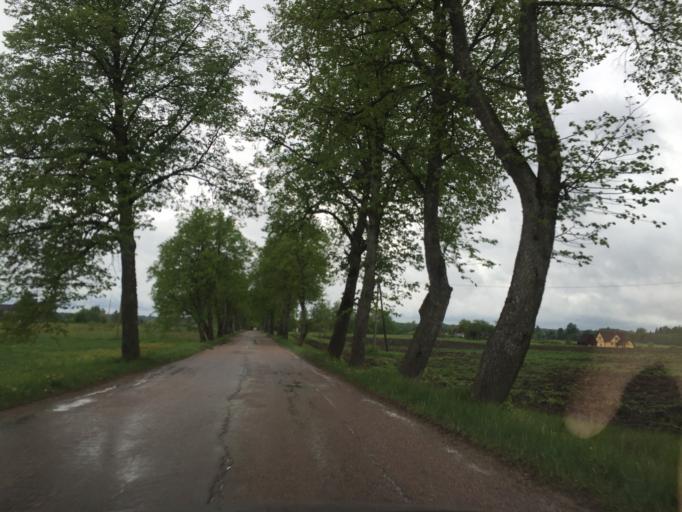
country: LV
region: Ogre
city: Jumprava
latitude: 56.6515
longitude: 24.9289
